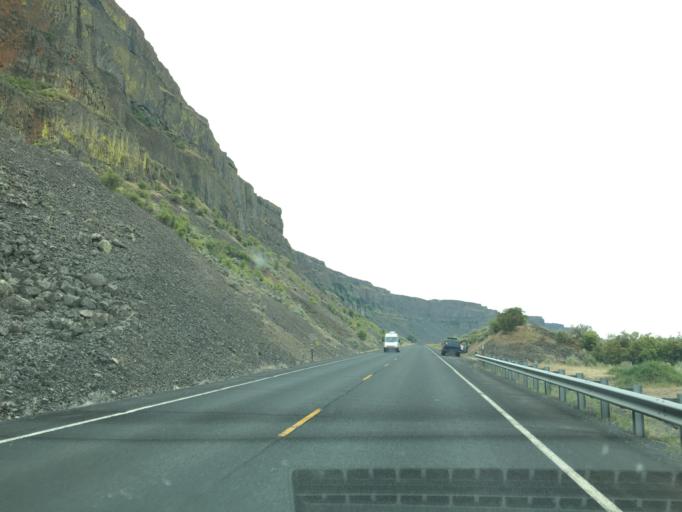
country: US
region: Washington
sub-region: Okanogan County
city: Coulee Dam
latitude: 47.8401
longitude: -119.1249
